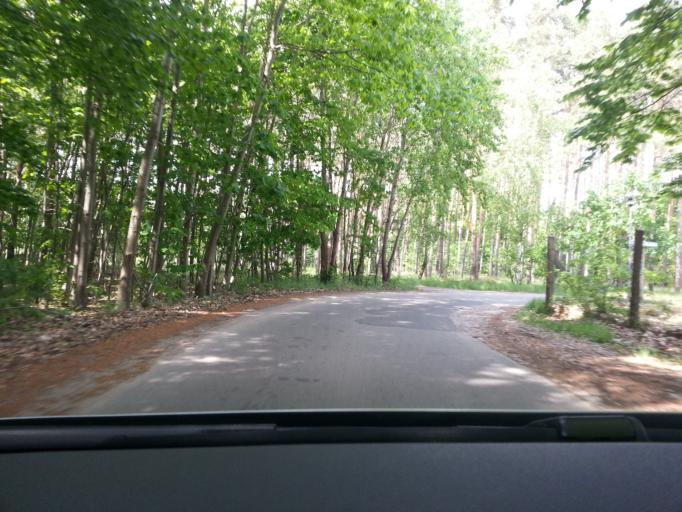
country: DE
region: Mecklenburg-Vorpommern
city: Torgelow
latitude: 53.6406
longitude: 13.9987
